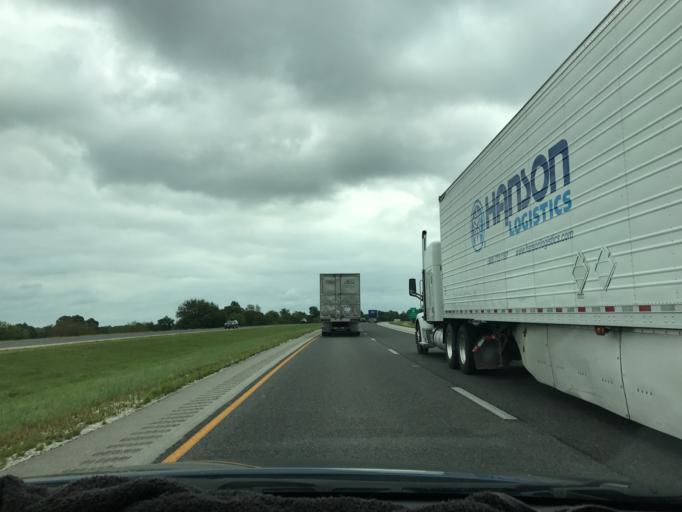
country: US
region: Illinois
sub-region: Henry County
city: Geneseo
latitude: 41.4404
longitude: -90.1789
